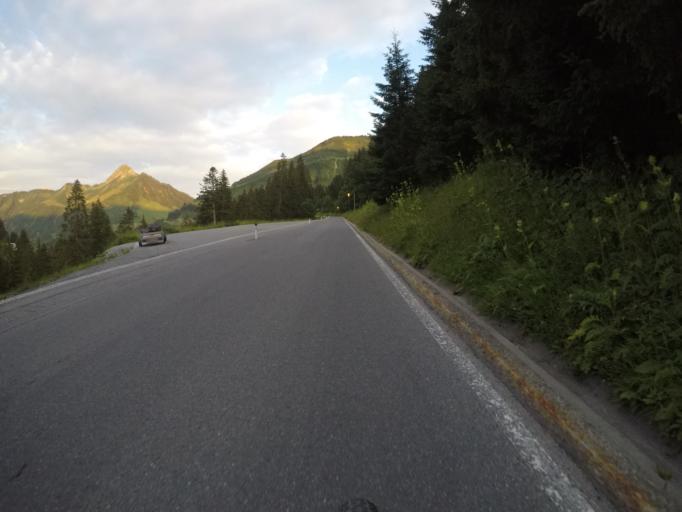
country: AT
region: Vorarlberg
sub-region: Politischer Bezirk Bregenz
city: Damuels
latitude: 47.2848
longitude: 9.8877
